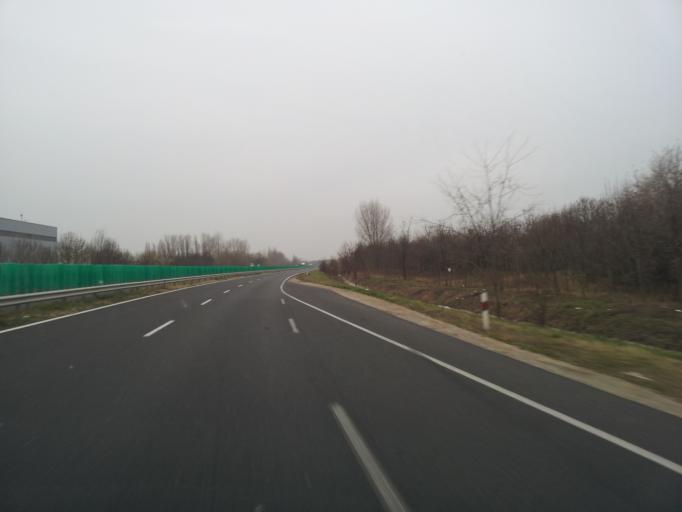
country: HU
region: Fejer
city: Szekesfehervar
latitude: 47.1476
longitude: 18.4189
